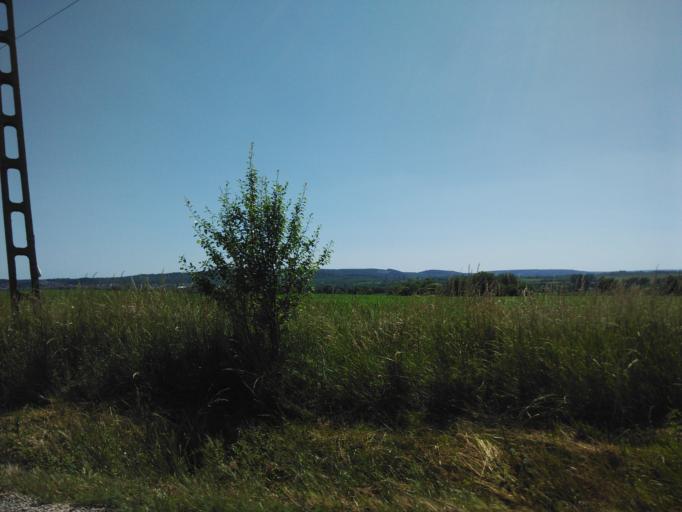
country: HU
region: Fejer
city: Bodajk
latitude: 47.3461
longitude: 18.2314
